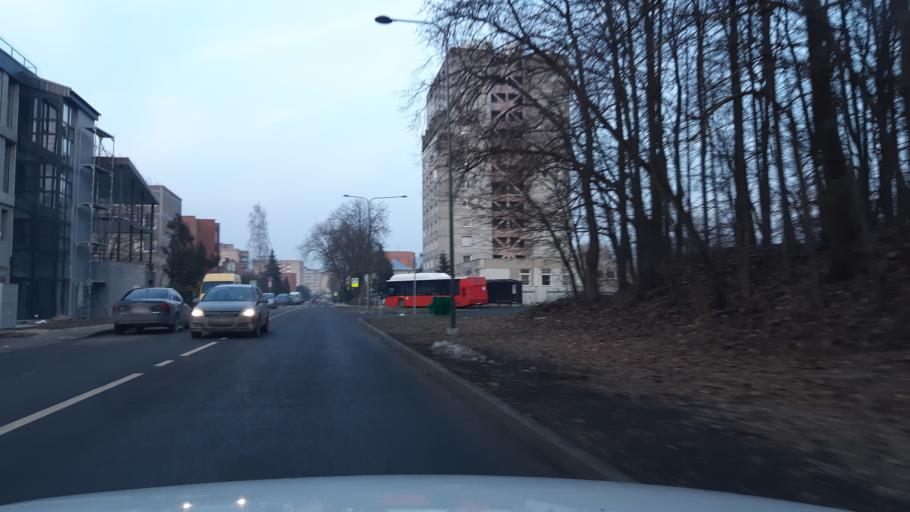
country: LT
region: Kauno apskritis
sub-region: Kaunas
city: Aleksotas
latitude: 54.8870
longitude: 23.9392
